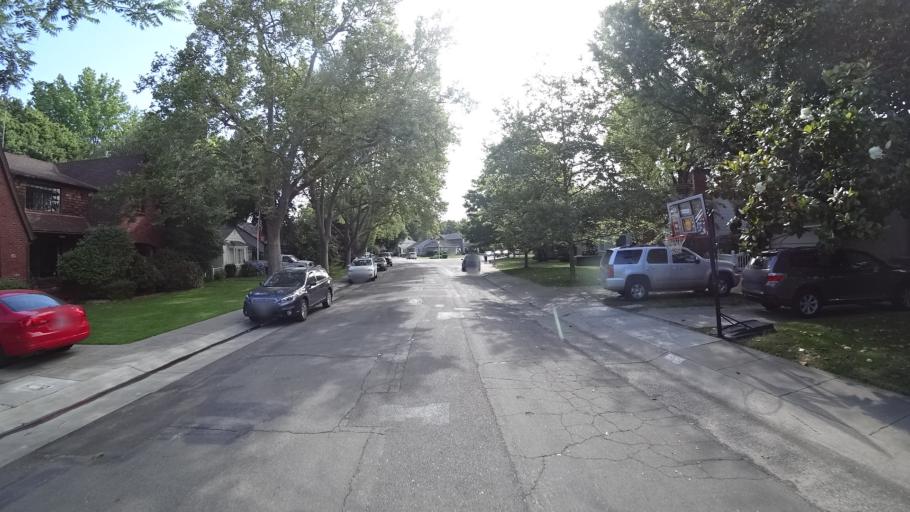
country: US
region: California
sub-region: Sacramento County
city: Sacramento
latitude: 38.5538
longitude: -121.5015
